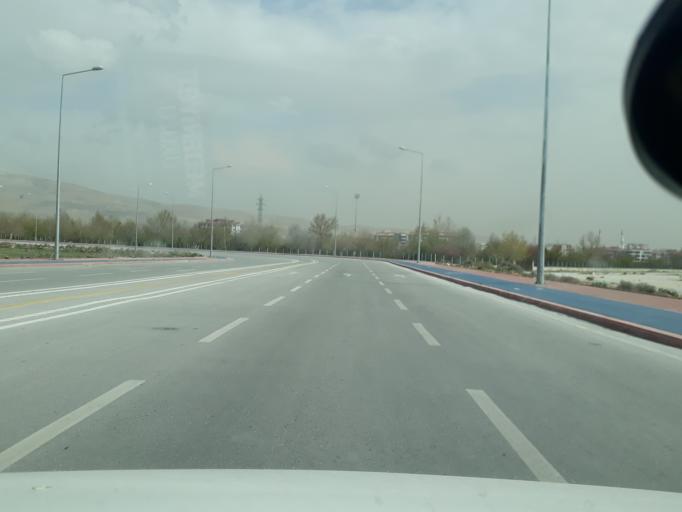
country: TR
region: Konya
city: Selcuklu
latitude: 37.9452
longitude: 32.4804
